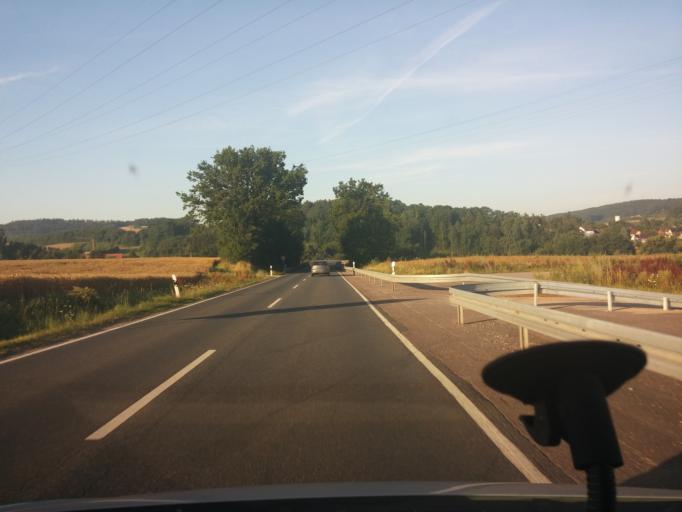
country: DE
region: Bavaria
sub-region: Regierungsbezirk Unterfranken
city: Sailauf
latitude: 50.0015
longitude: 9.2415
